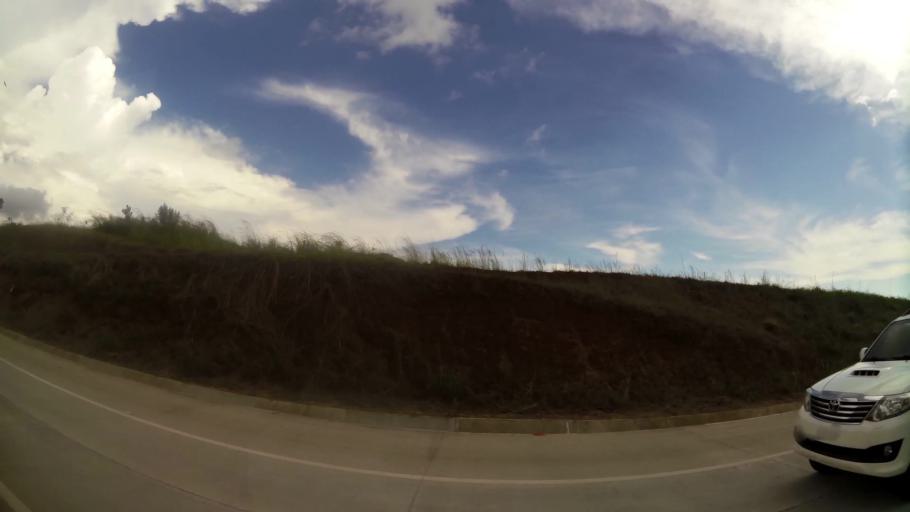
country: PA
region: Panama
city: Tocumen
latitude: 9.1023
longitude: -79.4145
